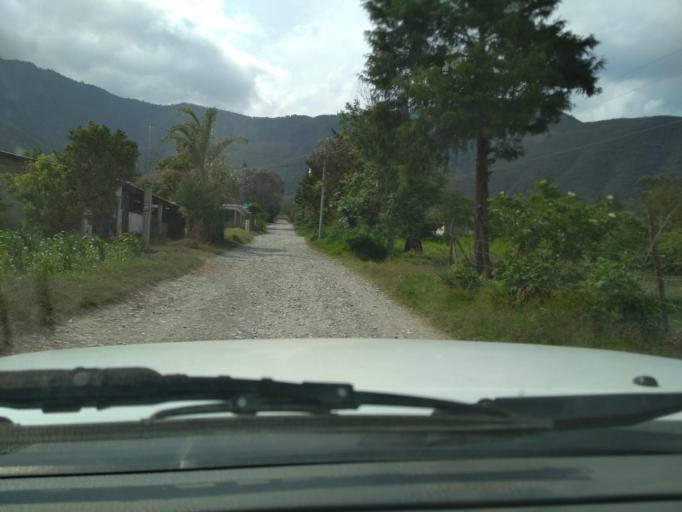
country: MX
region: Veracruz
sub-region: Acultzingo
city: Acatla
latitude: 18.7672
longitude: -97.2281
